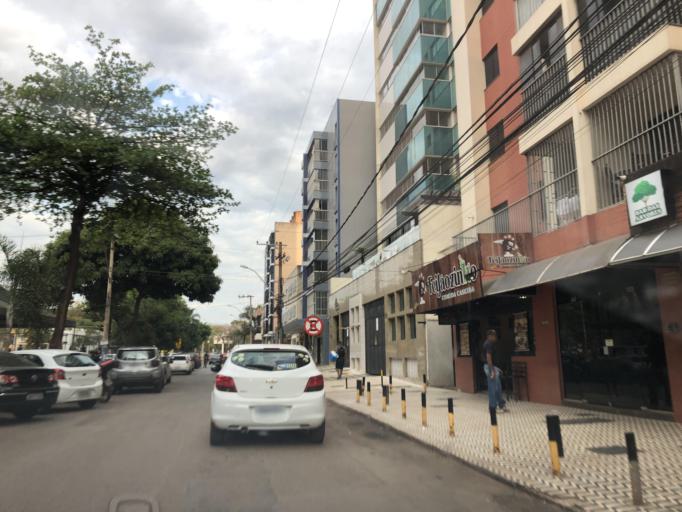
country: BR
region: Federal District
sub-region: Brasilia
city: Brasilia
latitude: -15.8349
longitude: -48.0511
